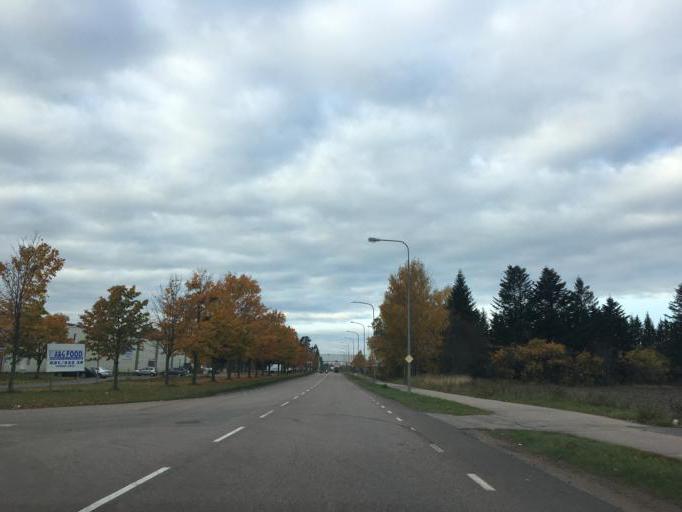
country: SE
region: Vaestmanland
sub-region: Vasteras
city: Vasteras
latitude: 59.5896
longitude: 16.4918
